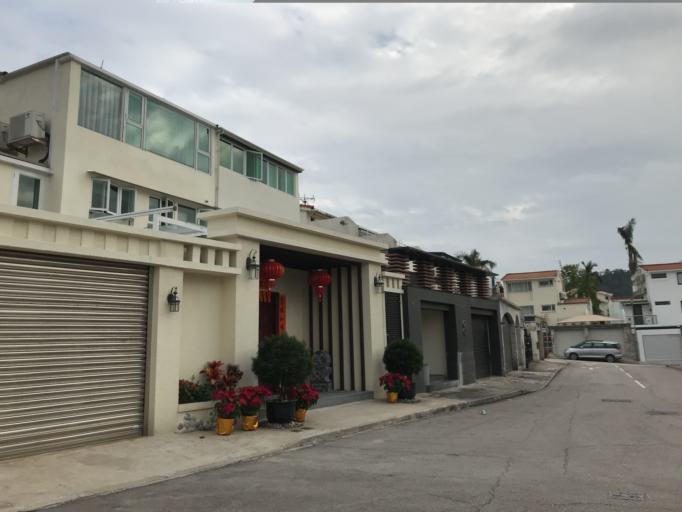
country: HK
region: Tai Po
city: Tai Po
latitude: 22.4659
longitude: 114.1568
